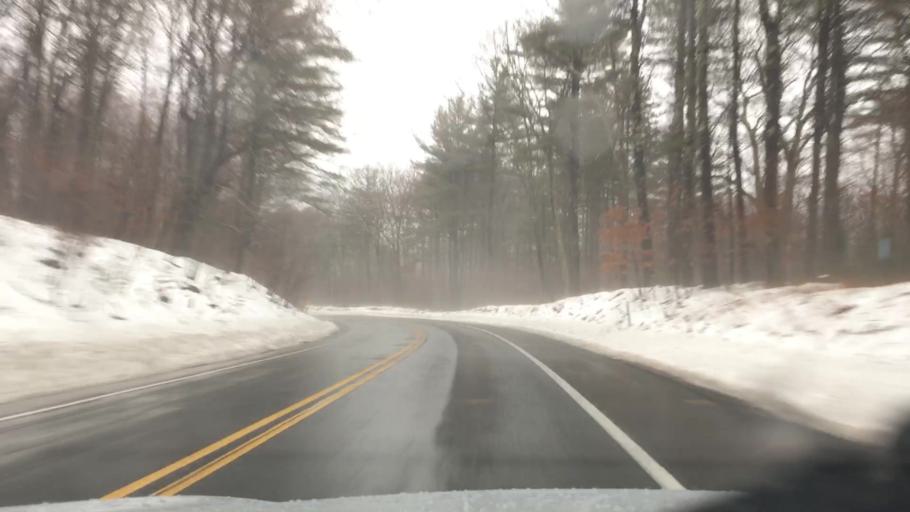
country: US
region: Massachusetts
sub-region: Hampshire County
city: Pelham
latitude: 42.4152
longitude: -72.3999
